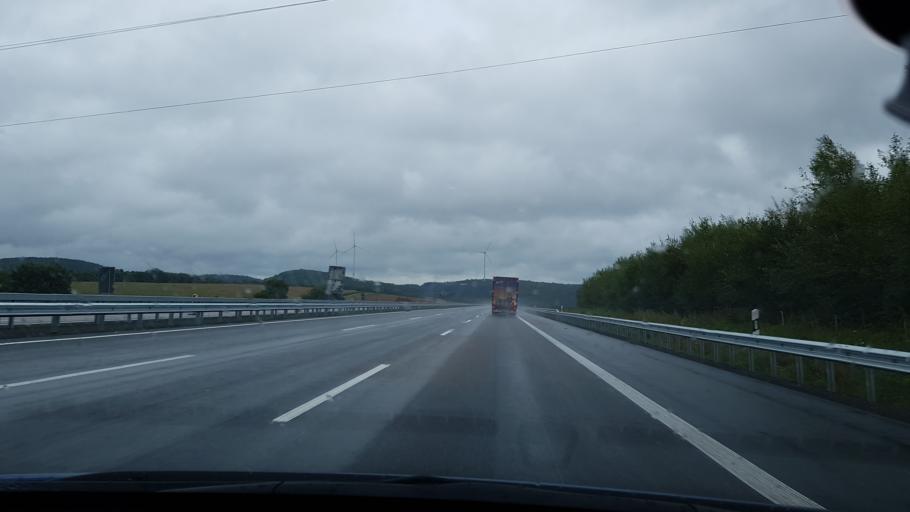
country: DE
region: Rheinland-Pfalz
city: Kaiserslautern
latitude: 49.4599
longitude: 7.7790
